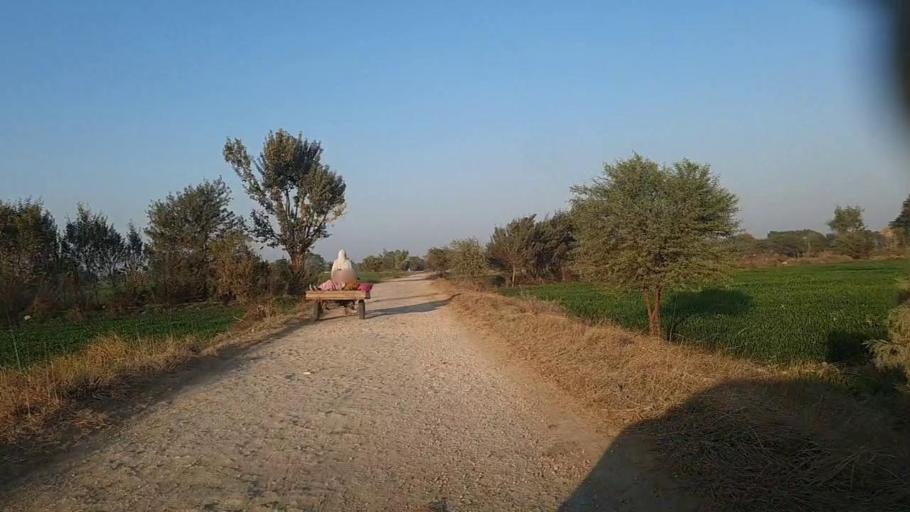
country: PK
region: Sindh
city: Mirpur Mathelo
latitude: 27.8829
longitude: 69.6526
